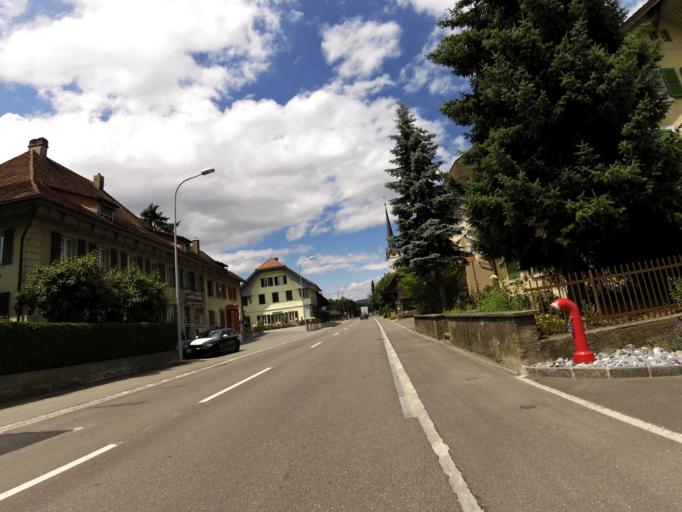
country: CH
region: Bern
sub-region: Oberaargau
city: Aarwangen
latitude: 47.2416
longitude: 7.7677
